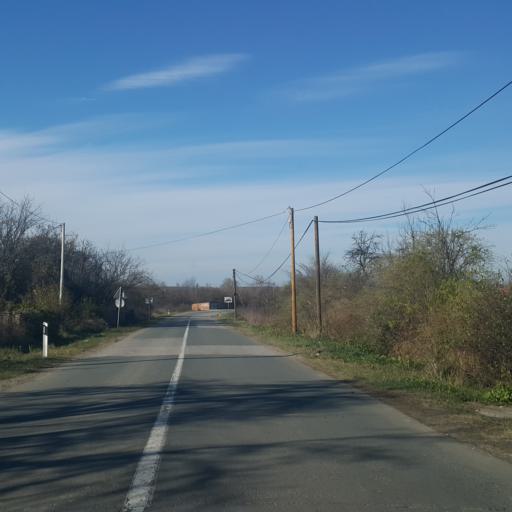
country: RS
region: Central Serbia
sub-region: Sumadijski Okrug
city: Raca
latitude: 44.2413
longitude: 20.8326
